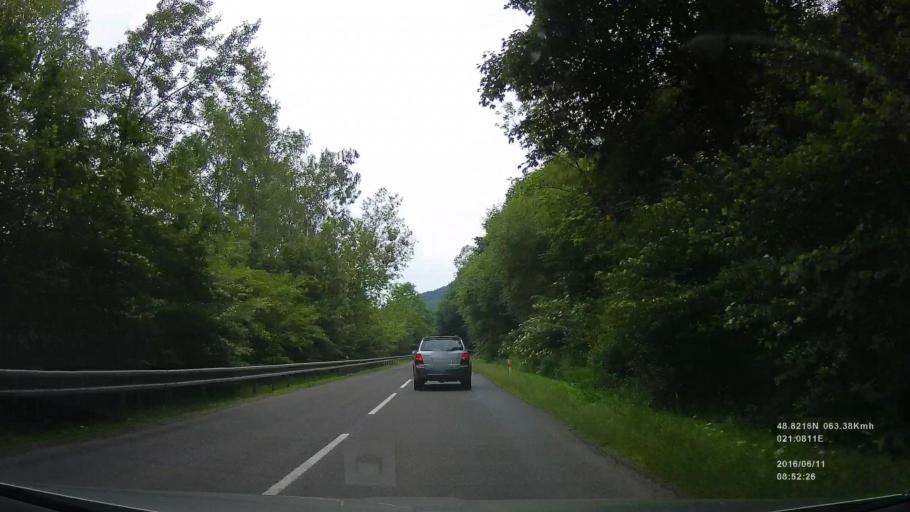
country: SK
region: Kosicky
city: Gelnica
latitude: 48.8169
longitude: 21.0856
